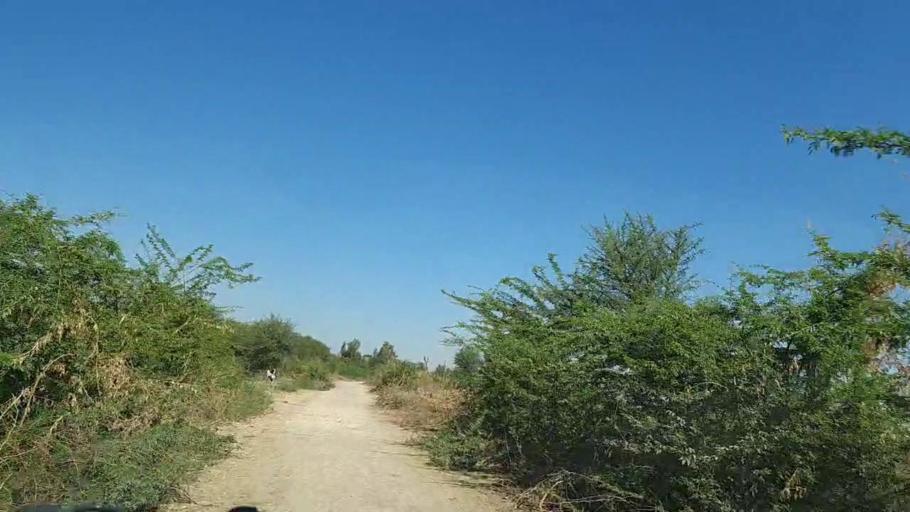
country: PK
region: Sindh
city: Dhoro Naro
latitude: 25.4741
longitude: 69.5129
